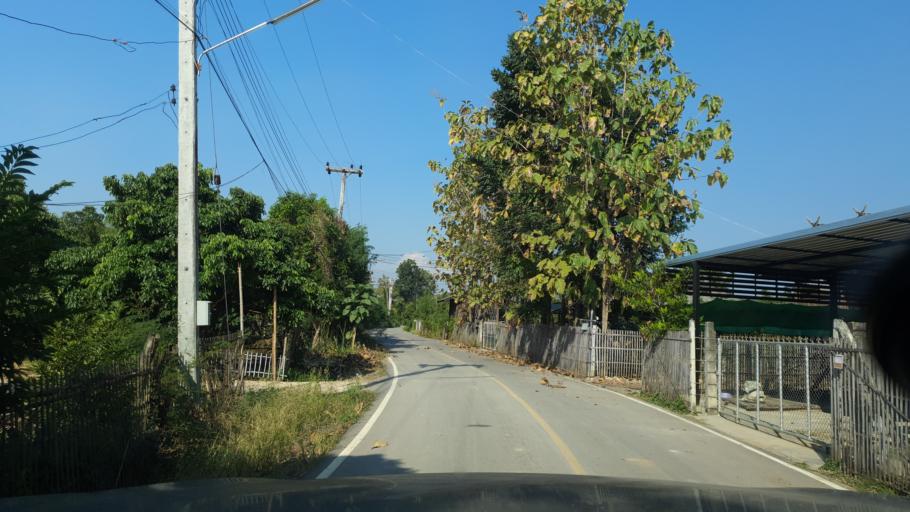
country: TH
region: Lamphun
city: Ban Thi
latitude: 18.6859
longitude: 99.0979
